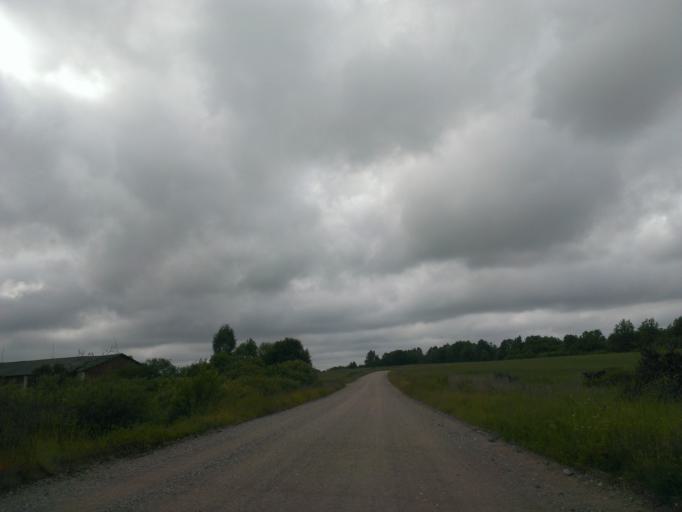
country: LV
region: Durbe
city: Liegi
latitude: 56.7446
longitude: 21.4056
